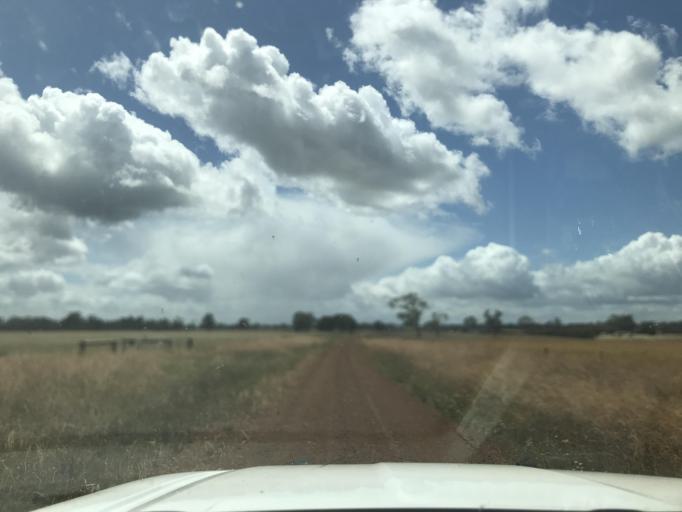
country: AU
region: South Australia
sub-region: Wattle Range
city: Penola
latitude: -37.1833
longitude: 141.4625
